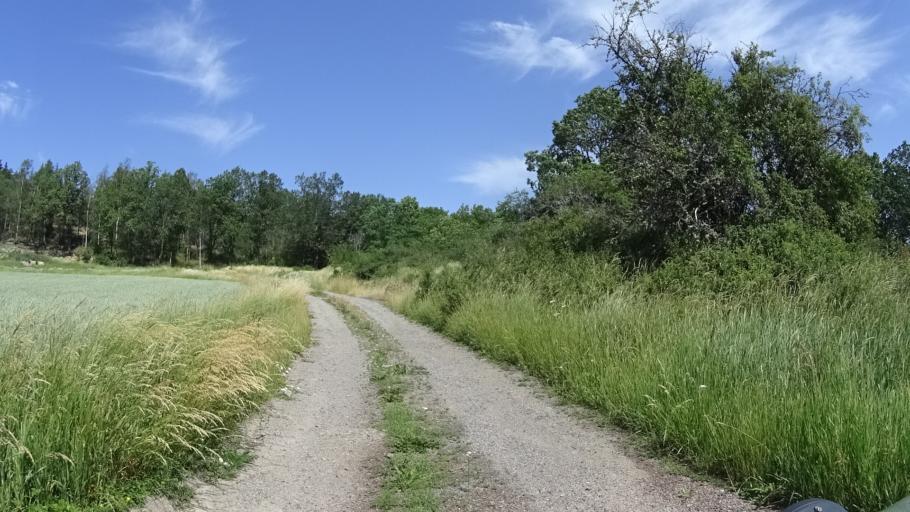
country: SE
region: Kalmar
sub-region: Vasterviks Kommun
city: Gamleby
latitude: 57.9186
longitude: 16.4066
